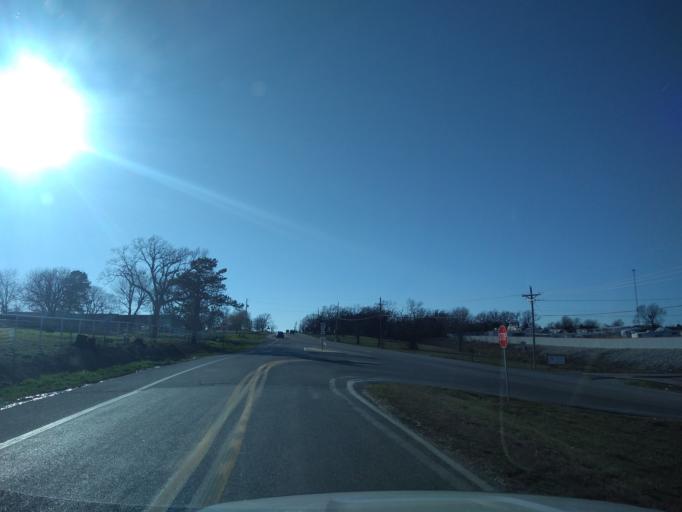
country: US
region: Arkansas
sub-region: Washington County
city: Lincoln
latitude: 35.9509
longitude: -94.3783
